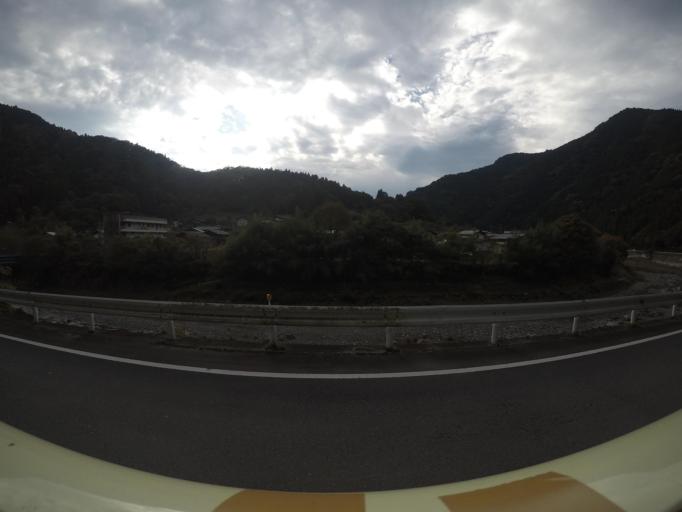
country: JP
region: Gunma
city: Yoshii
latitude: 36.1202
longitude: 138.9390
